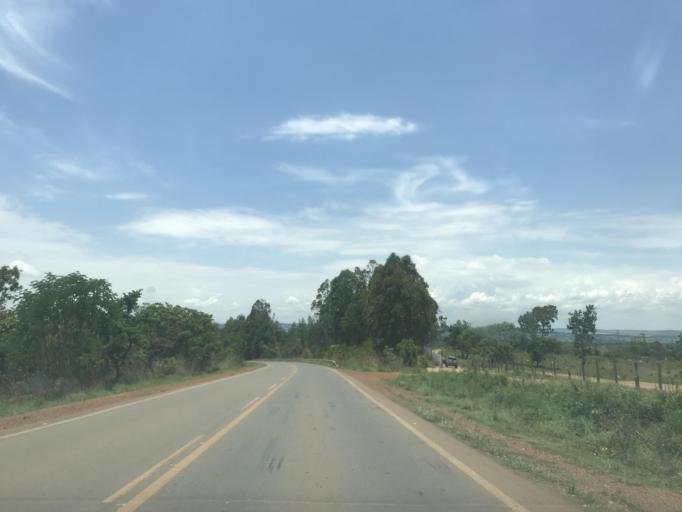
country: BR
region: Goias
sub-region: Vianopolis
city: Vianopolis
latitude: -16.5984
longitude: -48.3485
